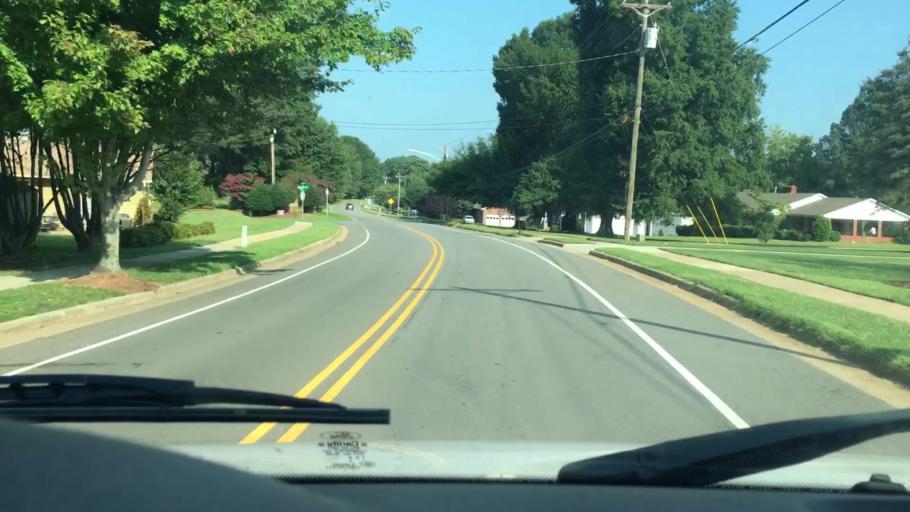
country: US
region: North Carolina
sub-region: Mecklenburg County
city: Cornelius
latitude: 35.4987
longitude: -80.8852
